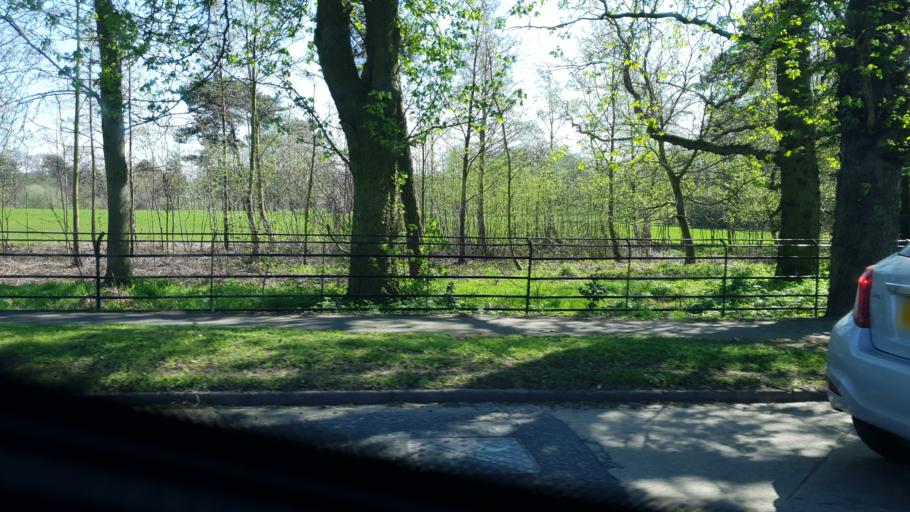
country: GB
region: England
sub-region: Middlesbrough
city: Nunthorpe
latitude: 54.5409
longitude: -1.2100
